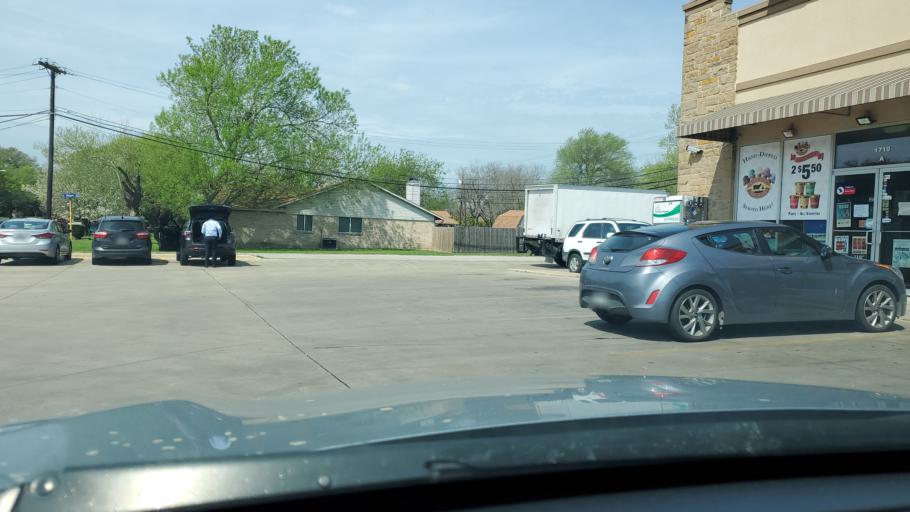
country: US
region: Texas
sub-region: Bell County
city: Temple
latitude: 31.0621
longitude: -97.3745
